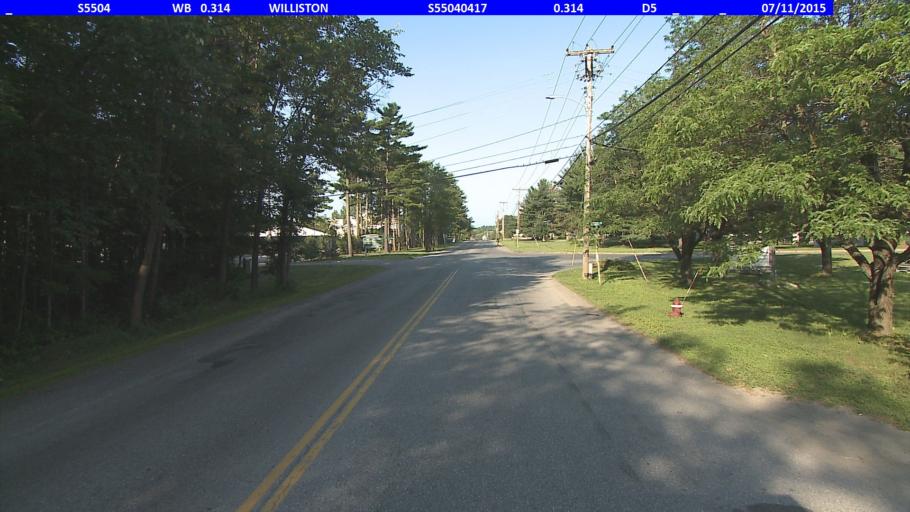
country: US
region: Vermont
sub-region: Chittenden County
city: Essex Junction
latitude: 44.4607
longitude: -73.1256
